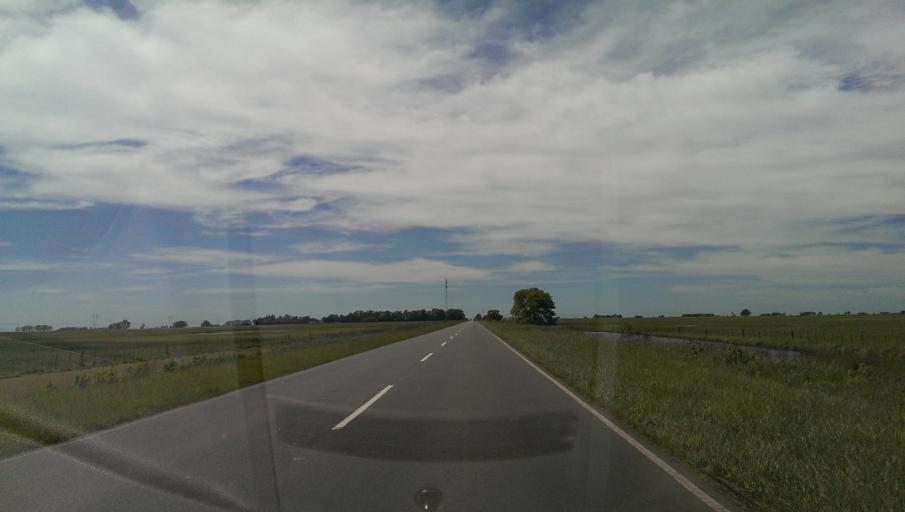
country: AR
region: Buenos Aires
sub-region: Partido de Laprida
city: Laprida
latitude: -37.1992
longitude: -60.6689
